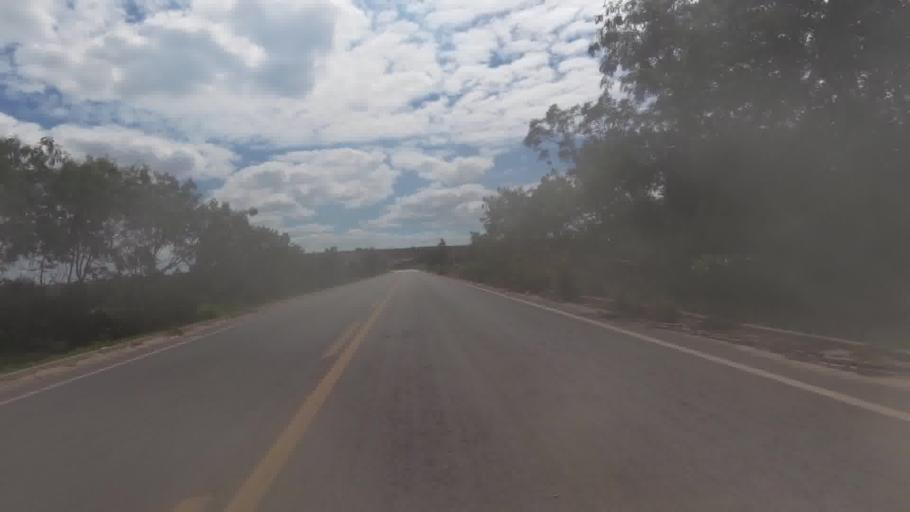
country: BR
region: Espirito Santo
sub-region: Marataizes
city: Marataizes
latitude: -21.2059
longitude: -40.9660
